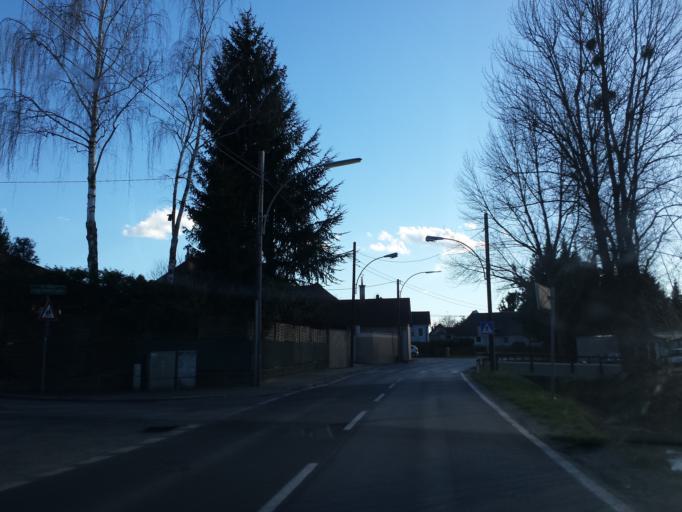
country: AT
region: Styria
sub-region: Politischer Bezirk Graz-Umgebung
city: Stattegg
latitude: 47.1198
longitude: 15.4377
